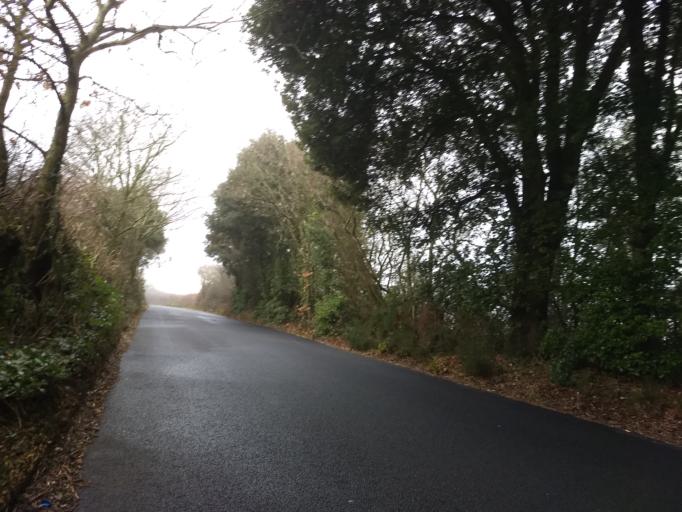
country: GB
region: England
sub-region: Isle of Wight
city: Newport
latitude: 50.7051
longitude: -1.2577
